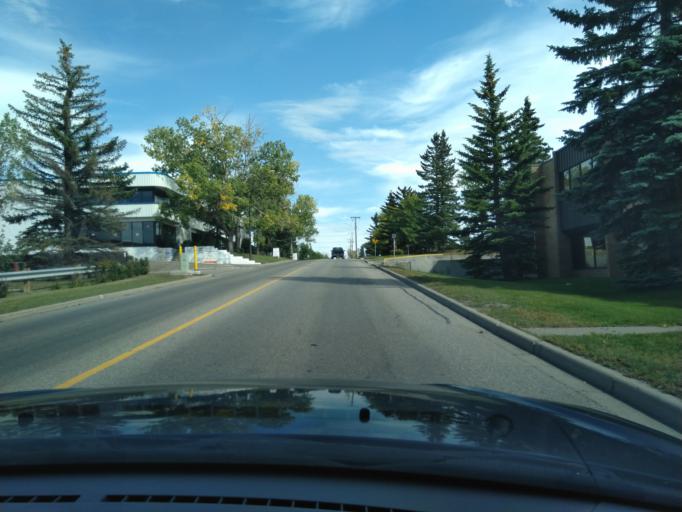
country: CA
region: Alberta
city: Calgary
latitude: 51.0769
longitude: -114.0245
